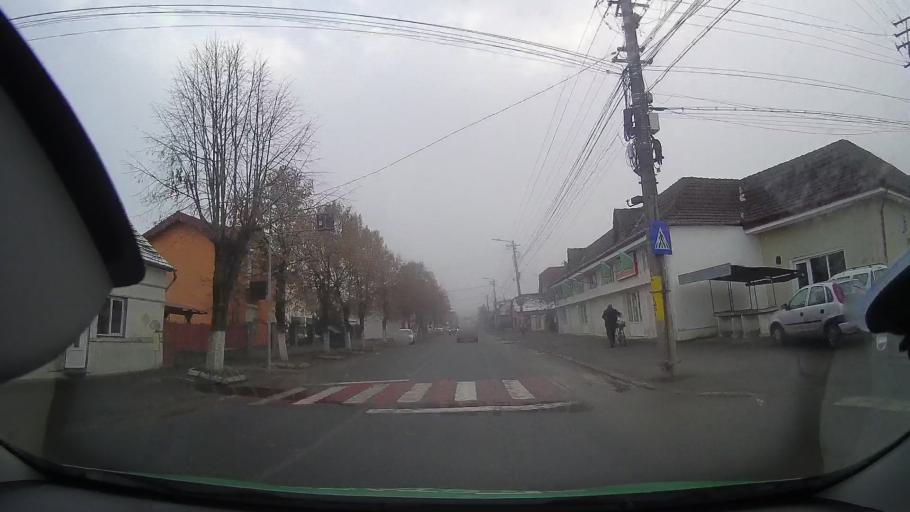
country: RO
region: Mures
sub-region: Municipiul Tarnaveni
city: Tarnaveni
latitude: 46.3194
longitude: 24.2965
